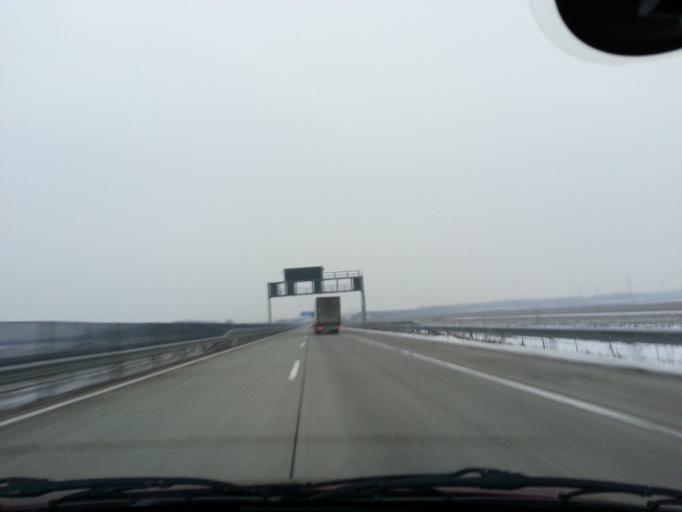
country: HU
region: Pest
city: Nagytarcsa
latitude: 47.5157
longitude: 19.3001
